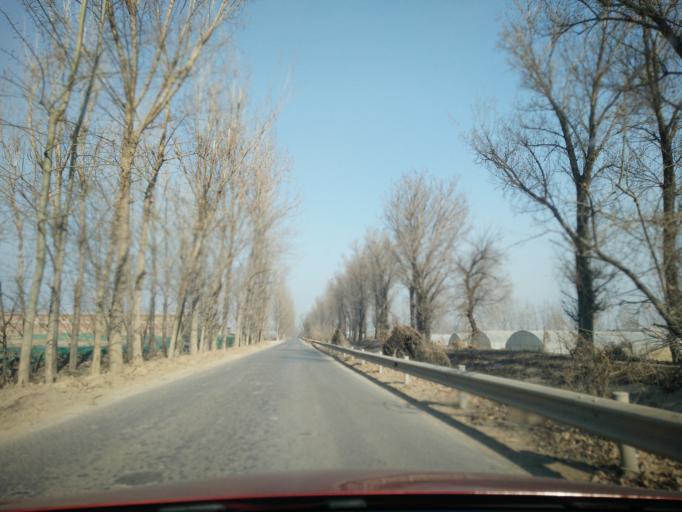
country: CN
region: Beijing
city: Yinghai
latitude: 39.7123
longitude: 116.4467
